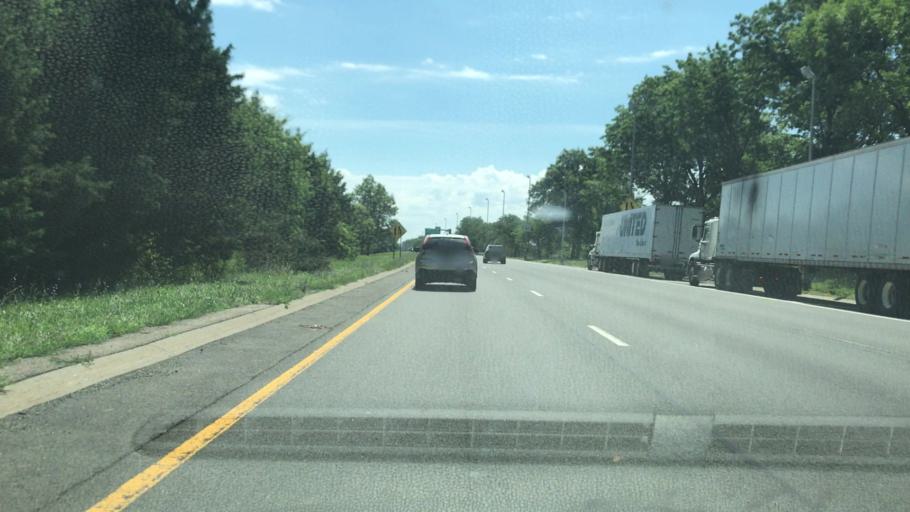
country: US
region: New York
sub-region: Bronx
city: The Bronx
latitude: 40.8212
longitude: -73.8168
